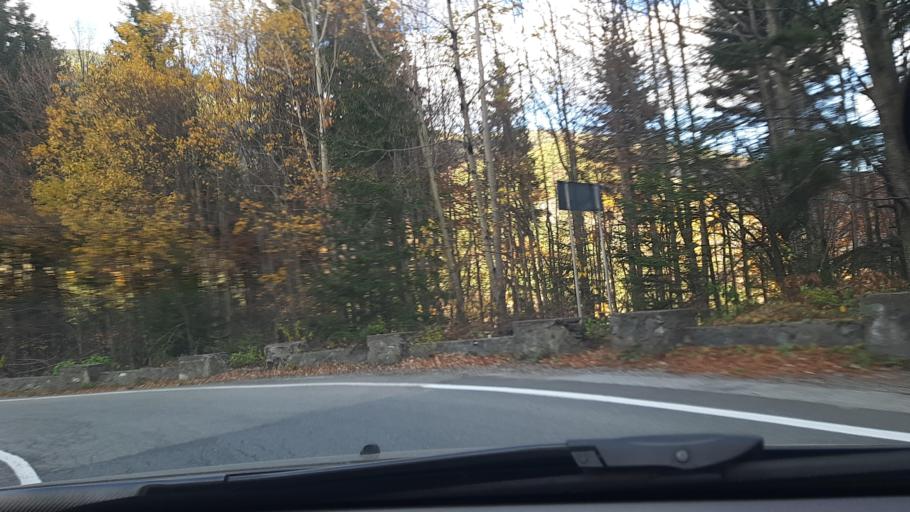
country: RO
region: Valcea
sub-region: Comuna Voineasa
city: Voineasa
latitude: 45.4338
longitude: 23.8618
